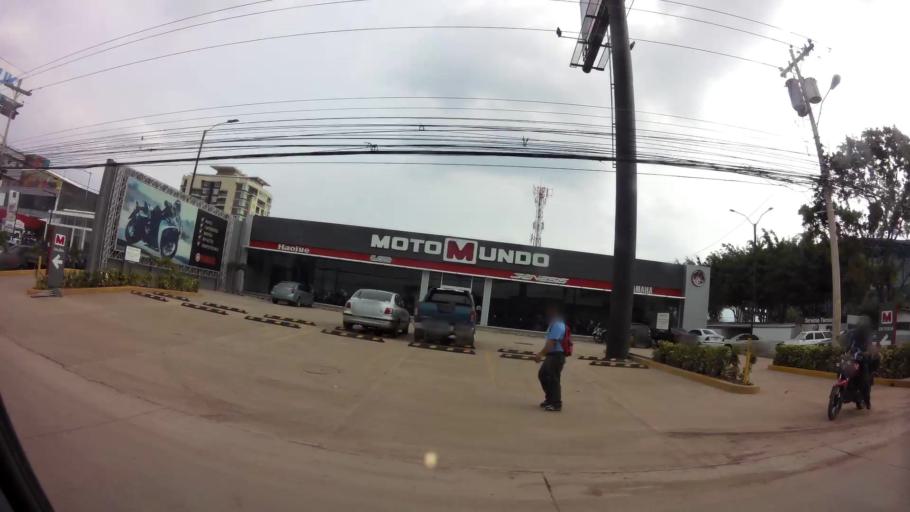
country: HN
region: Francisco Morazan
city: Tegucigalpa
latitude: 14.0842
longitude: -87.1715
